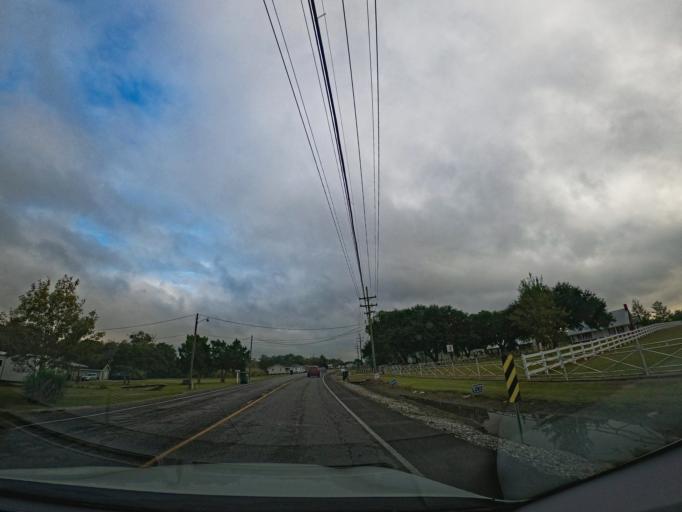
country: US
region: Louisiana
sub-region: Terrebonne Parish
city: Presquille
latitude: 29.4892
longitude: -90.6957
